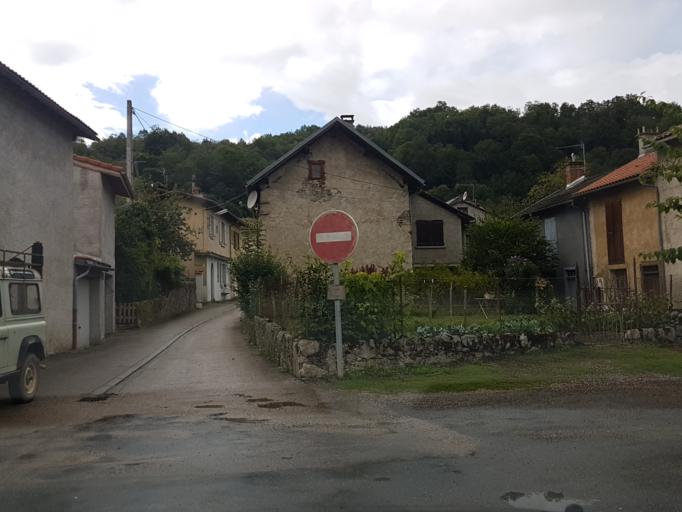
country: FR
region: Midi-Pyrenees
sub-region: Departement de l'Ariege
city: Saint-Girons
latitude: 42.8925
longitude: 1.2126
